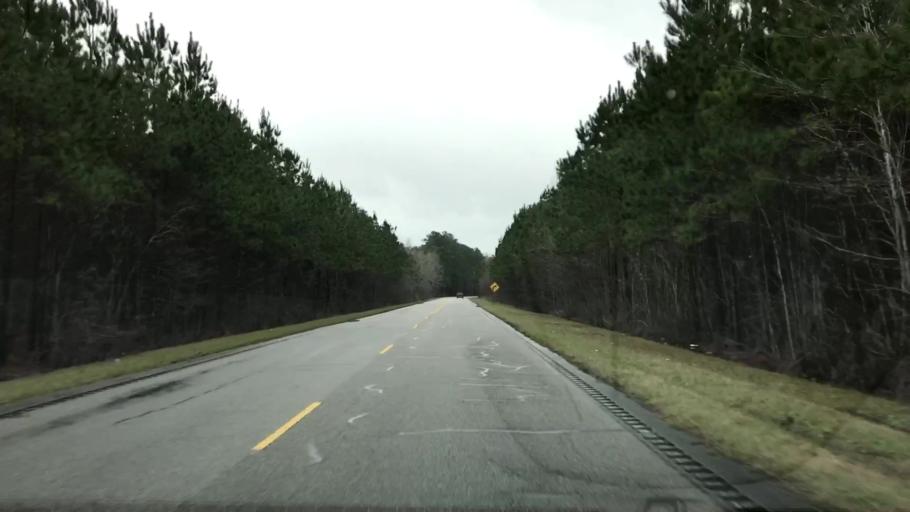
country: US
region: South Carolina
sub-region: Williamsburg County
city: Andrews
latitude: 33.5641
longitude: -79.4536
